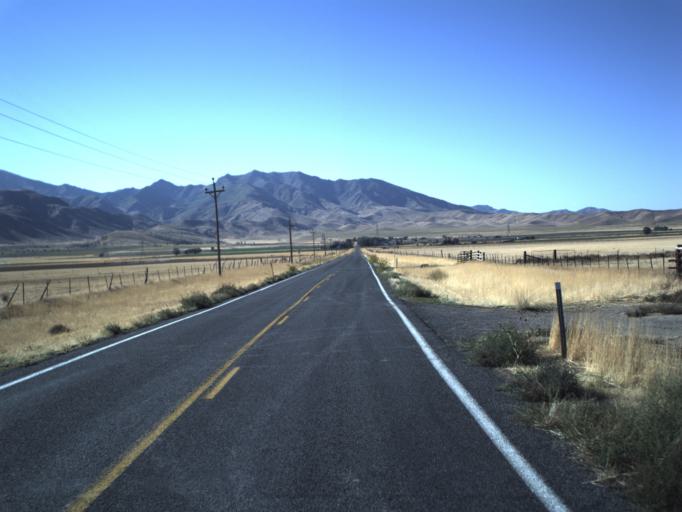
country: US
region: Utah
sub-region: Millard County
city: Delta
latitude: 39.5089
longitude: -112.2693
